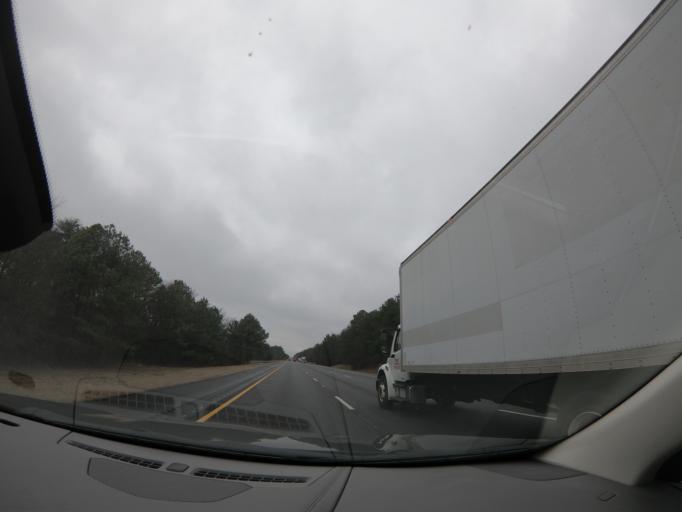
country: US
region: Georgia
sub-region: Whitfield County
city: Dalton
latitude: 34.8253
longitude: -85.0171
